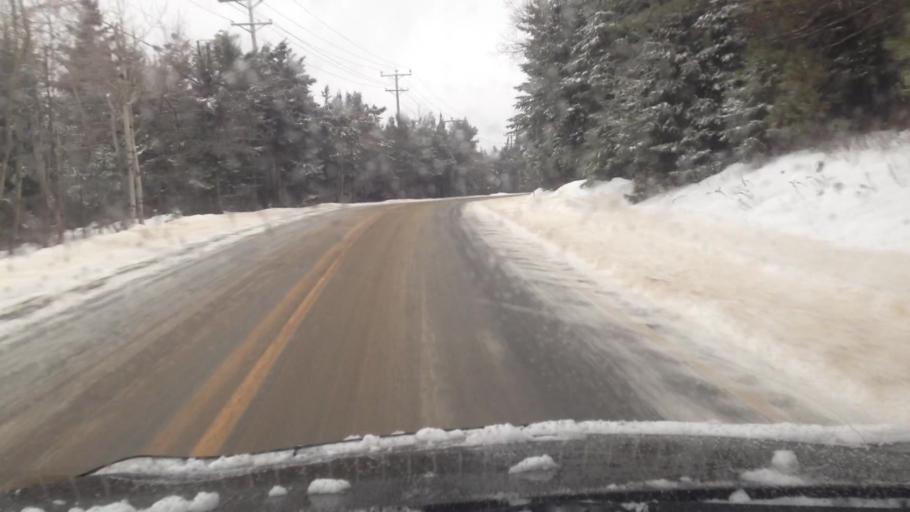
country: CA
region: Quebec
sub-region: Laurentides
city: Mont-Tremblant
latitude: 45.9985
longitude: -74.6240
